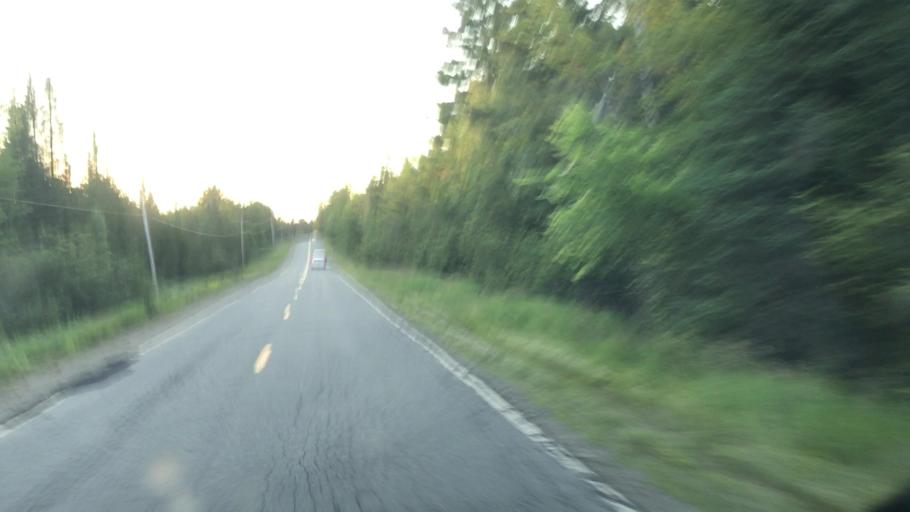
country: US
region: Maine
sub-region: Penobscot County
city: Medway
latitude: 45.6023
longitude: -68.2508
